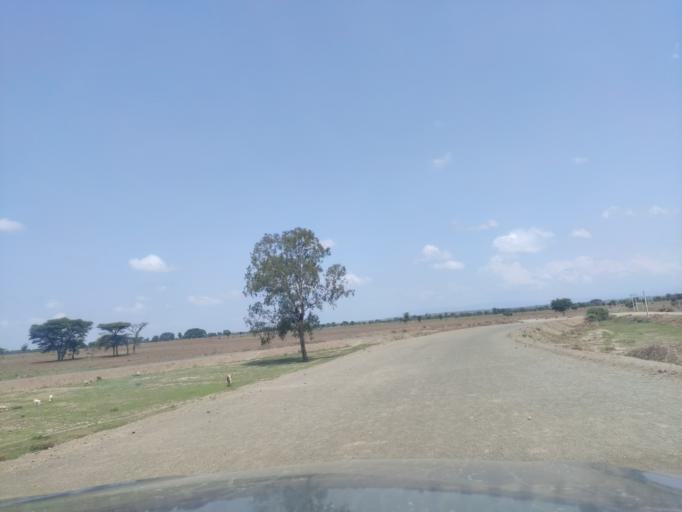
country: ET
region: Oromiya
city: Mojo
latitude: 8.3028
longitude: 38.9338
